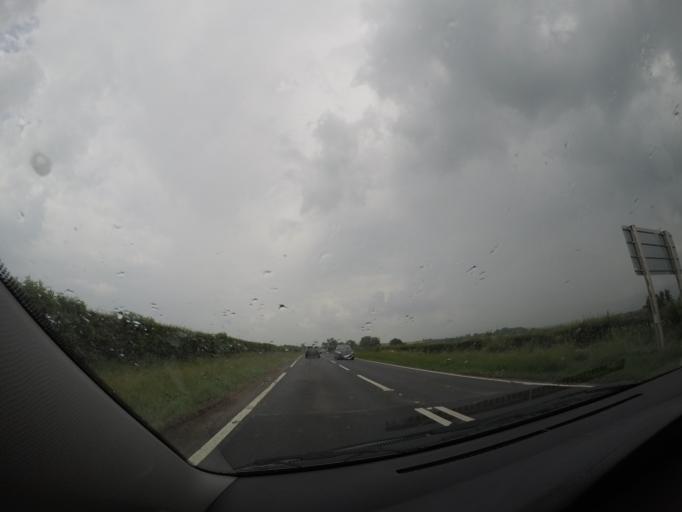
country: GB
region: England
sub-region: Cumbria
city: Appleby-in-Westmorland
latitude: 54.6084
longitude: -2.5425
